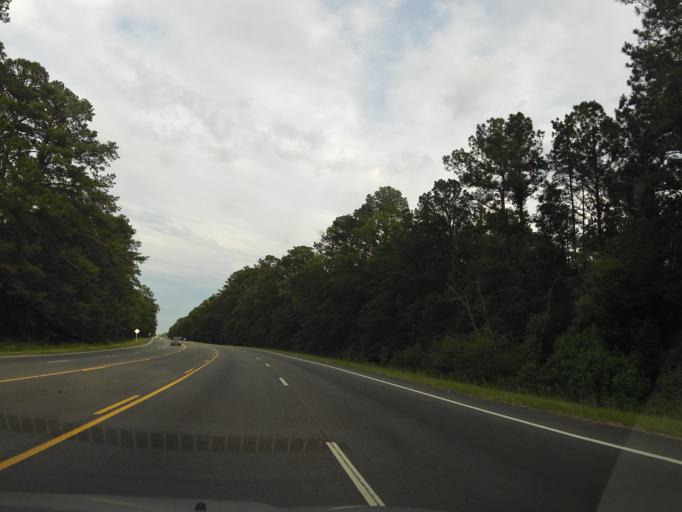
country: US
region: Georgia
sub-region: Chatham County
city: Pooler
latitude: 32.0976
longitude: -81.2189
